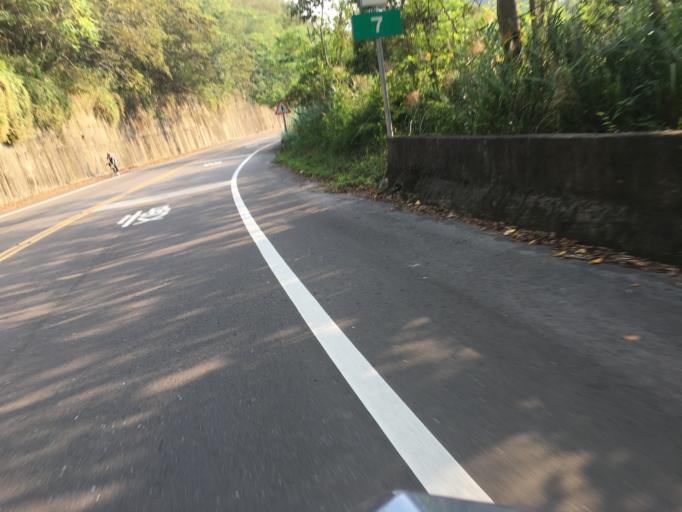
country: TW
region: Taiwan
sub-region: Hsinchu
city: Hsinchu
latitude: 24.7106
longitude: 121.0438
